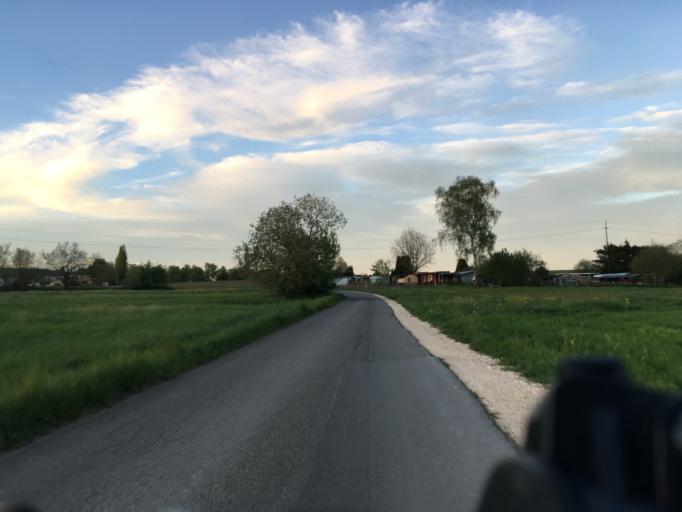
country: DE
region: Baden-Wuerttemberg
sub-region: Freiburg Region
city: Gottmadingen
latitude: 47.7236
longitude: 8.7743
